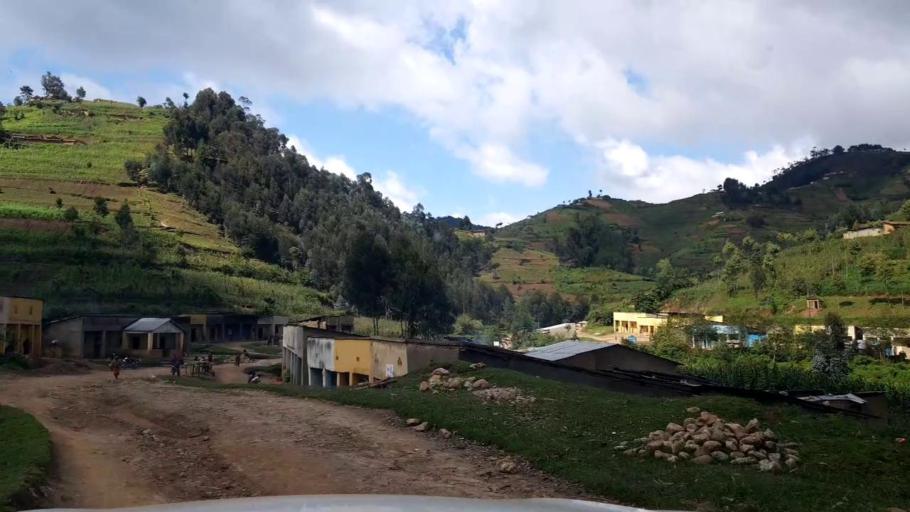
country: RW
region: Western Province
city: Kibuye
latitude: -1.8892
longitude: 29.4661
